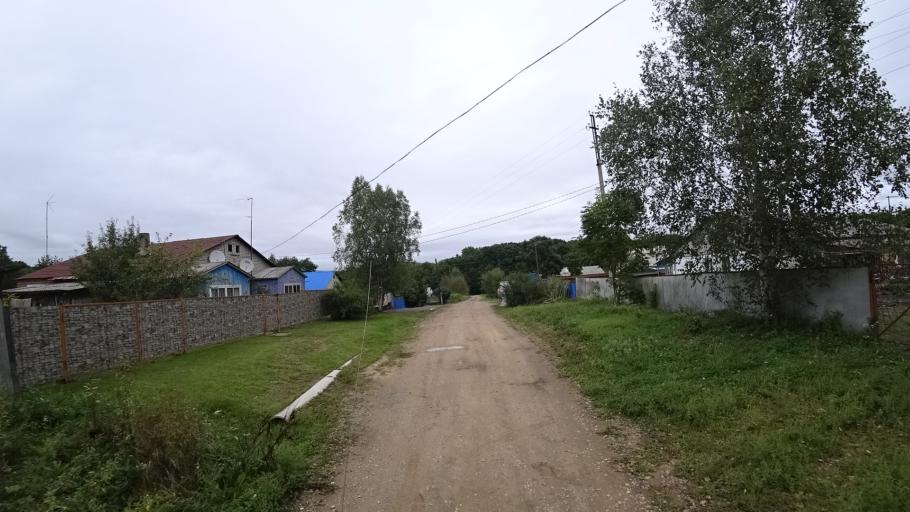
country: RU
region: Primorskiy
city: Rettikhovka
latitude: 44.1630
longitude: 132.7487
